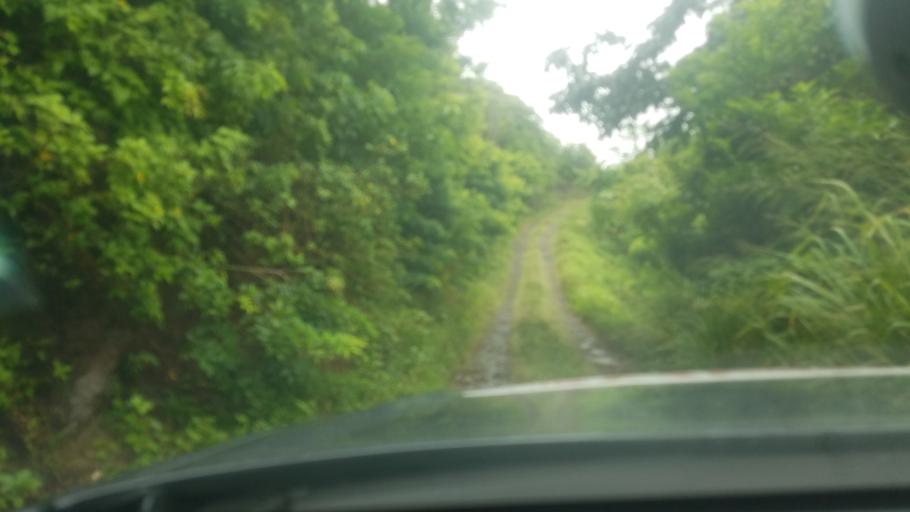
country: LC
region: Gros-Islet
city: Gros Islet
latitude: 14.0358
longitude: -60.9267
